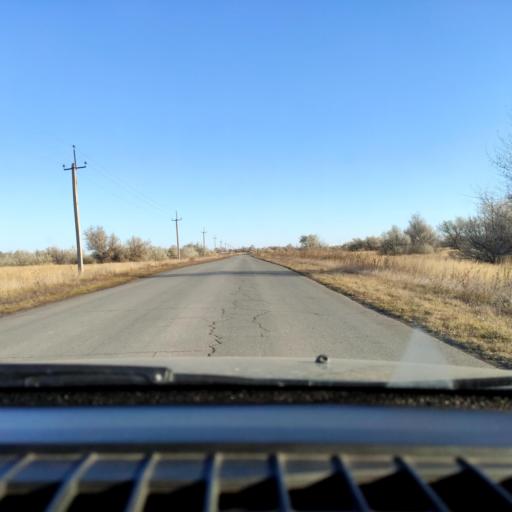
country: RU
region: Samara
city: Tol'yatti
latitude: 53.6526
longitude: 49.3255
